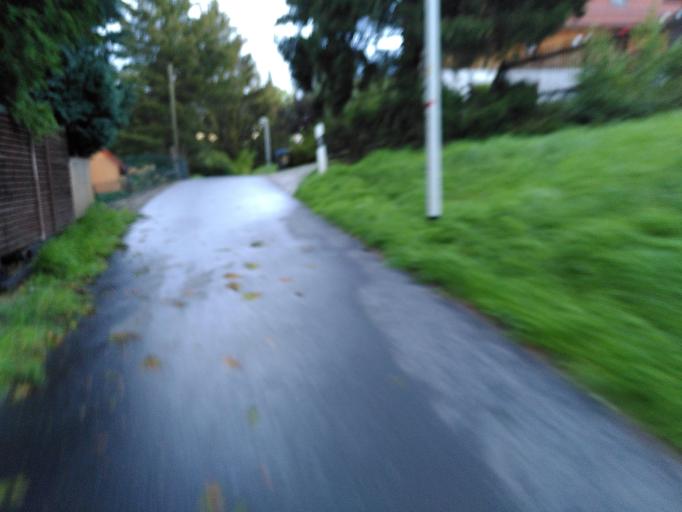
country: DE
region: Saxony
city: Radeberg
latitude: 51.0390
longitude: 13.9176
